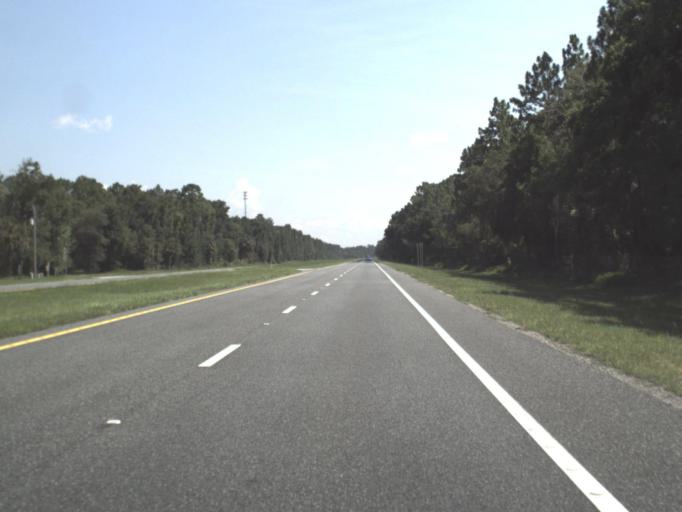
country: US
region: Florida
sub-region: Levy County
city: Inglis
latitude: 29.1079
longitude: -82.6364
